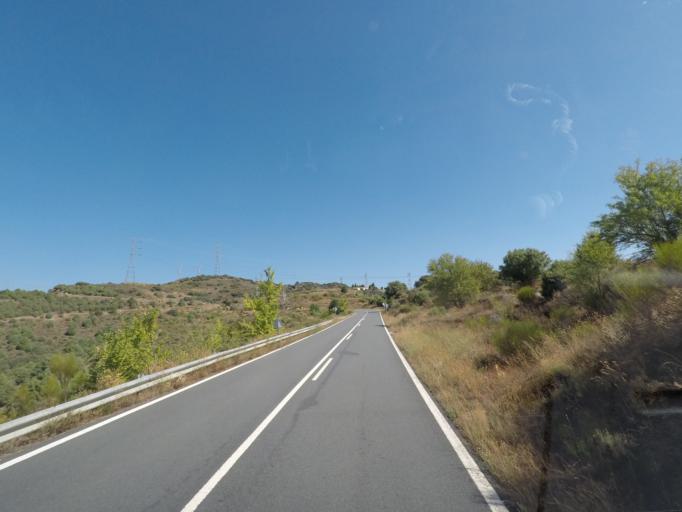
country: ES
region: Castille and Leon
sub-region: Provincia de Salamanca
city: Villarino de los Aires
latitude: 41.2991
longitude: -6.4820
